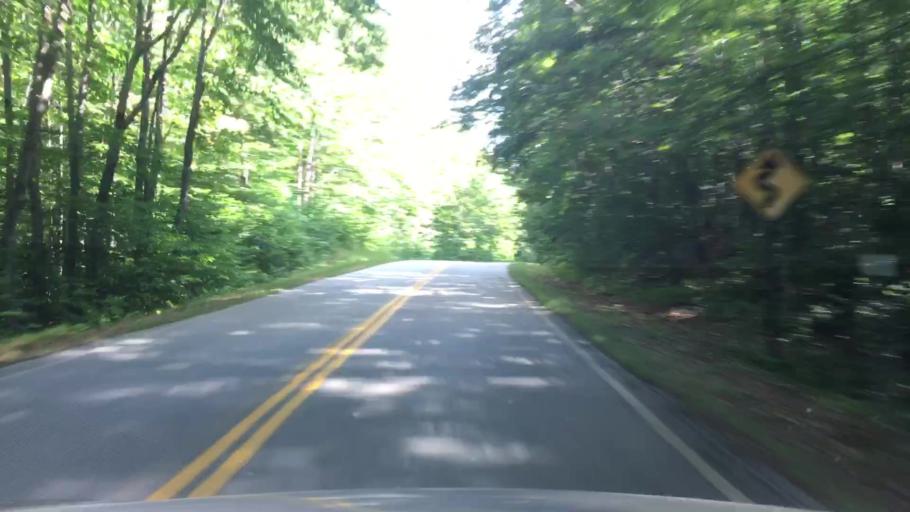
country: US
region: New Hampshire
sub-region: Carroll County
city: Tamworth
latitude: 44.0312
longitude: -71.3233
